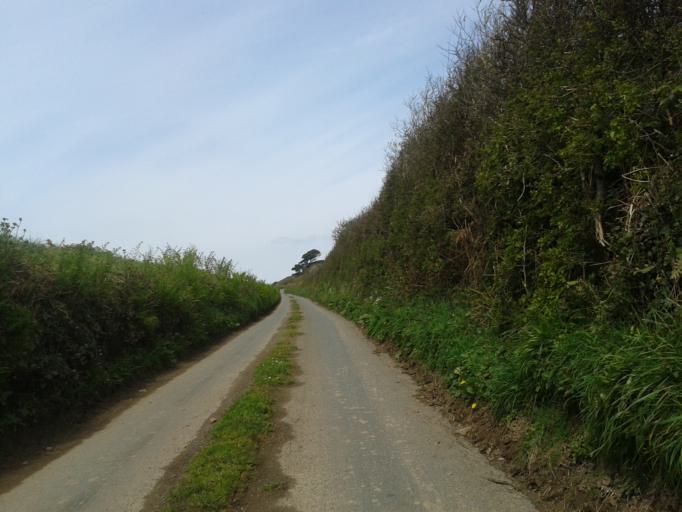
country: GB
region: England
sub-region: Devon
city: Braunton
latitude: 51.1425
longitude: -4.1862
